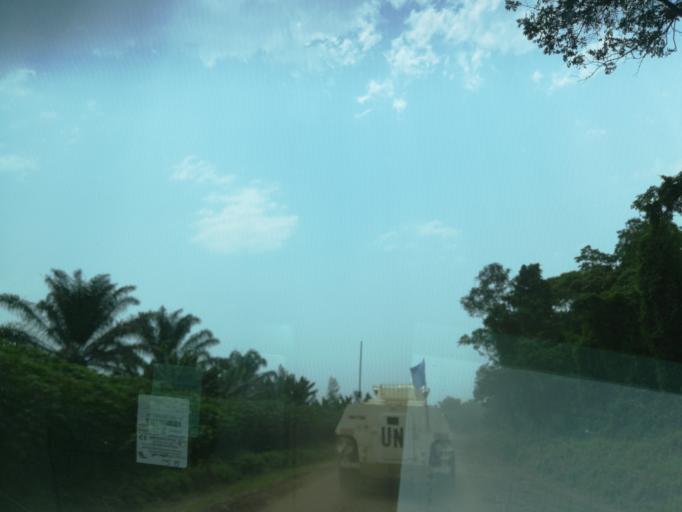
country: UG
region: Western Region
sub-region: Kasese District
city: Margherita
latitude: 0.2929
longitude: 29.6621
